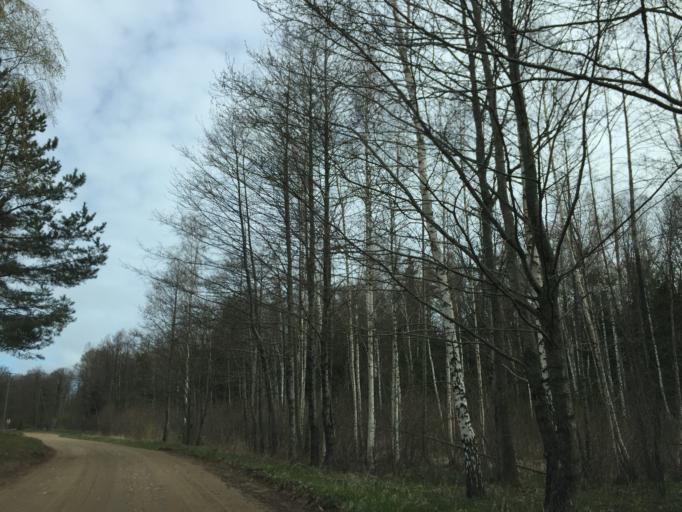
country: LV
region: Salacgrivas
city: Salacgriva
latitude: 57.5187
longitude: 24.3794
